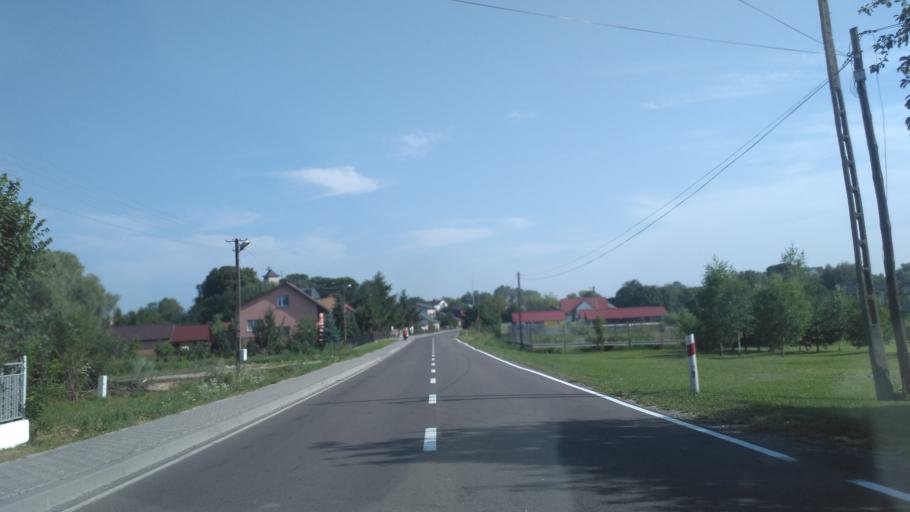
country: PL
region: Lublin Voivodeship
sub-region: Powiat leczynski
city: Cycow
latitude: 51.1917
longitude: 23.1631
